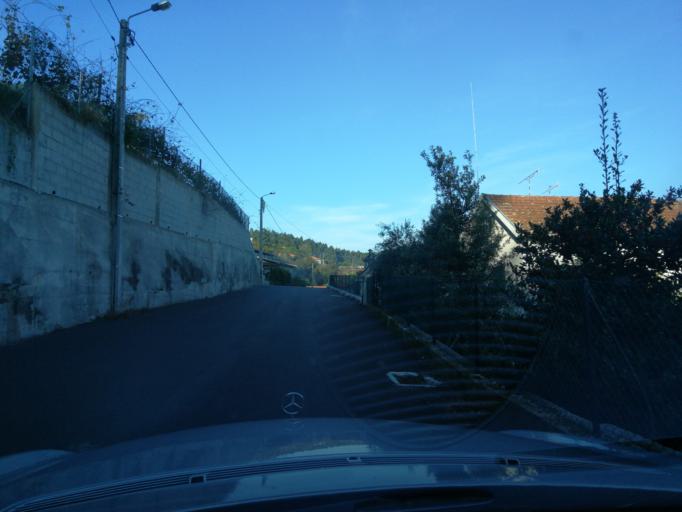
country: PT
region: Braga
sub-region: Braga
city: Oliveira
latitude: 41.4587
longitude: -8.4534
